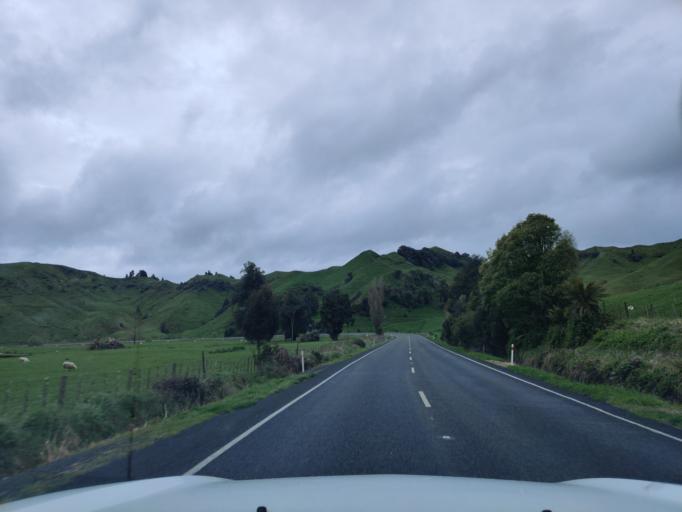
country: NZ
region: Waikato
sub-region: Otorohanga District
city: Otorohanga
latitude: -38.5550
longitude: 175.1950
